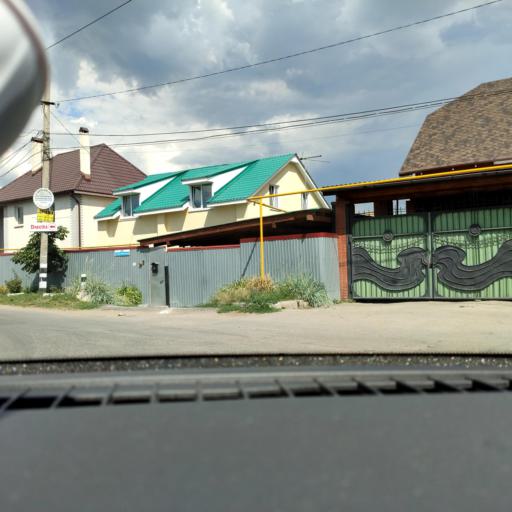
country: RU
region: Samara
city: Volzhskiy
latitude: 53.4268
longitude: 50.1234
